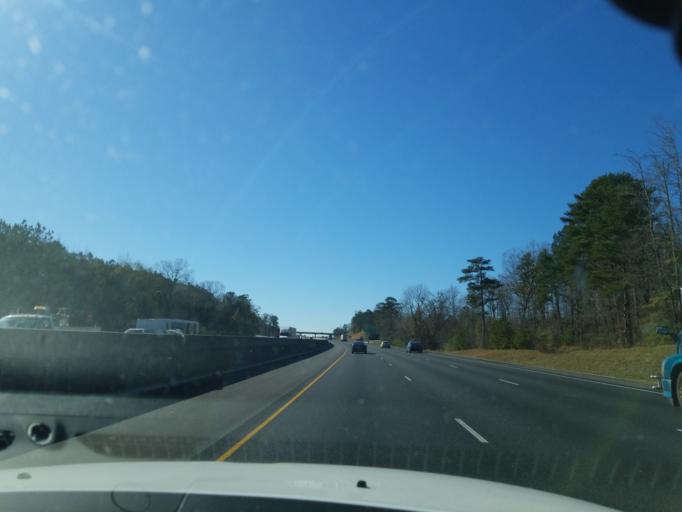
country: US
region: Alabama
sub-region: Tuscaloosa County
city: Lake View
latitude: 33.2839
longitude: -87.0902
